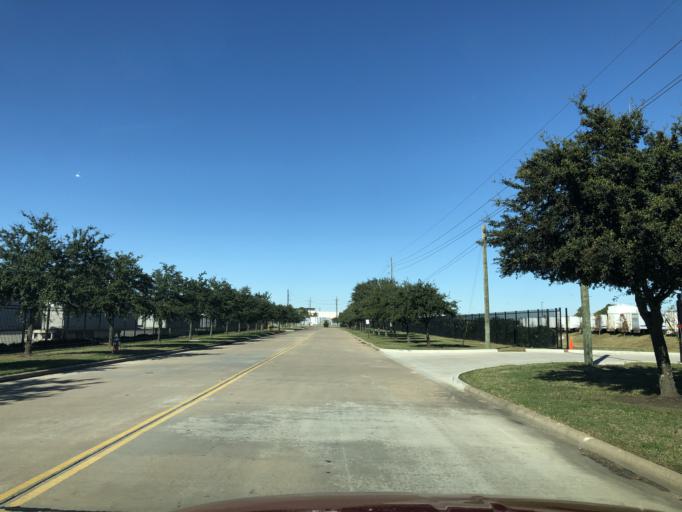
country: US
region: Texas
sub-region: Harris County
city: Oak Cliff Place
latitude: 29.9350
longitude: -95.6528
